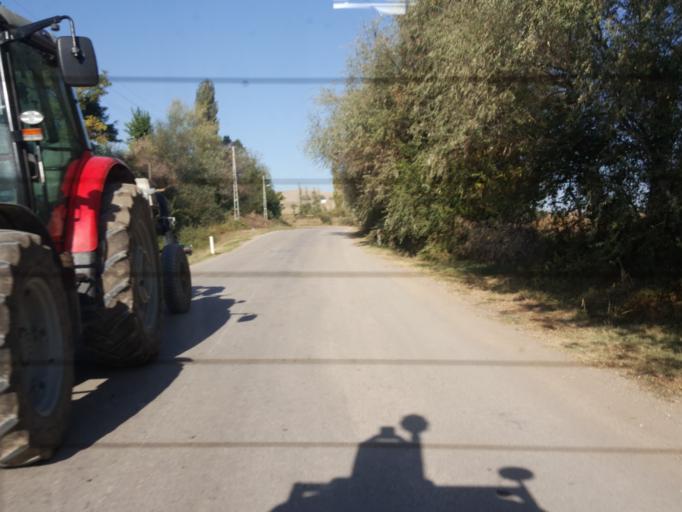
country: TR
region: Amasya
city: Saribugday
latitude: 40.7500
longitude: 35.4543
